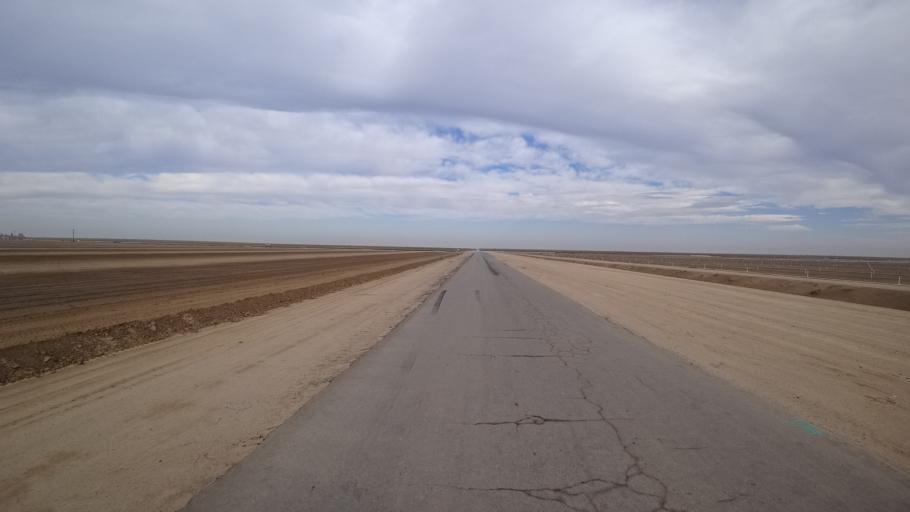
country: US
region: California
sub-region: Kern County
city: Rosedale
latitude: 35.4140
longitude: -119.1899
